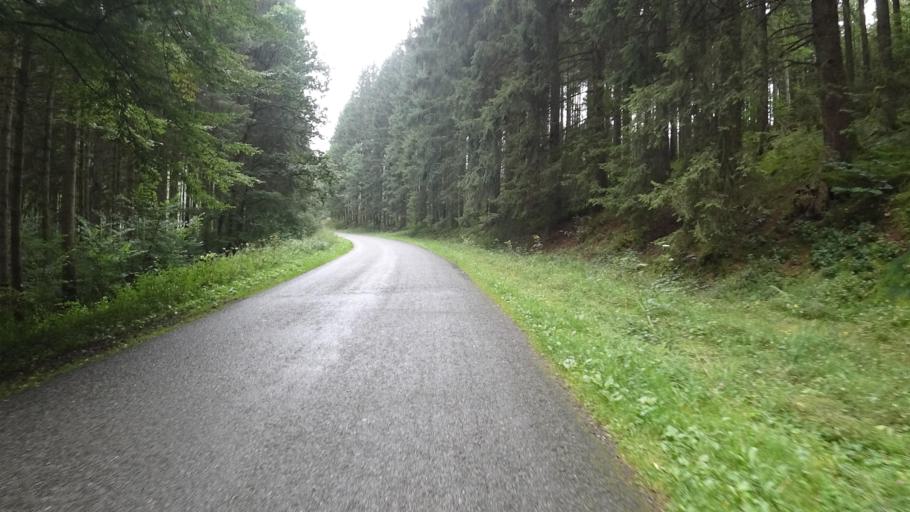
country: BE
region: Wallonia
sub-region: Province du Luxembourg
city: Chiny
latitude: 49.7867
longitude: 5.3722
